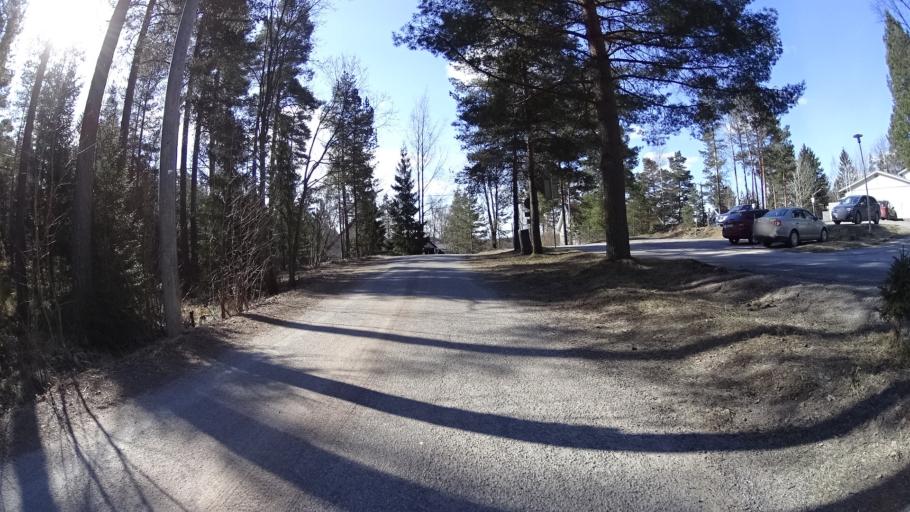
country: FI
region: Uusimaa
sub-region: Helsinki
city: Kilo
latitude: 60.2889
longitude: 24.7530
